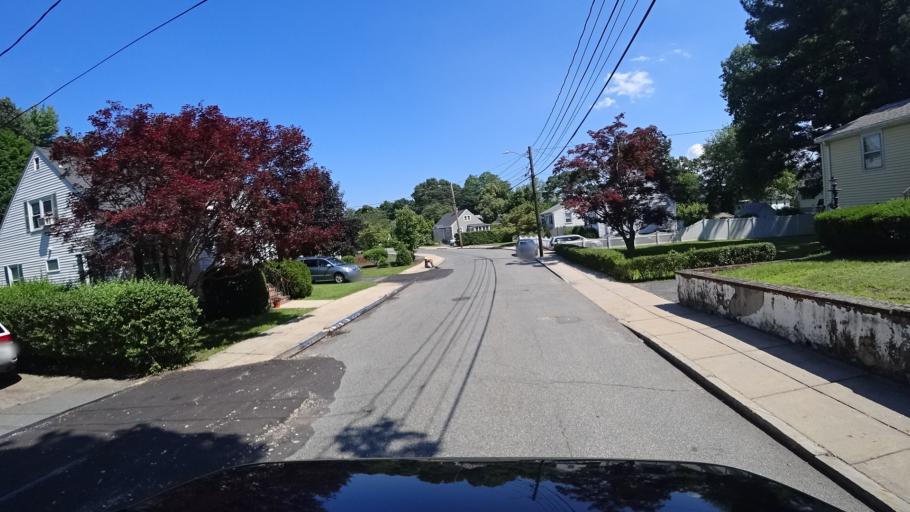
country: US
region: Massachusetts
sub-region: Norfolk County
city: Dedham
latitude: 42.2725
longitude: -71.1687
